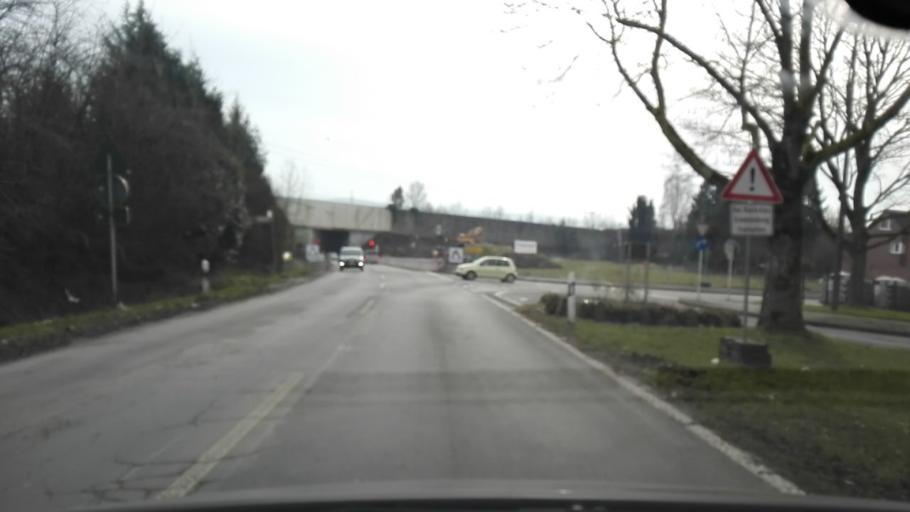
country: DE
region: North Rhine-Westphalia
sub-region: Regierungsbezirk Arnsberg
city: Holzwickede
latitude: 51.4736
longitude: 7.6005
